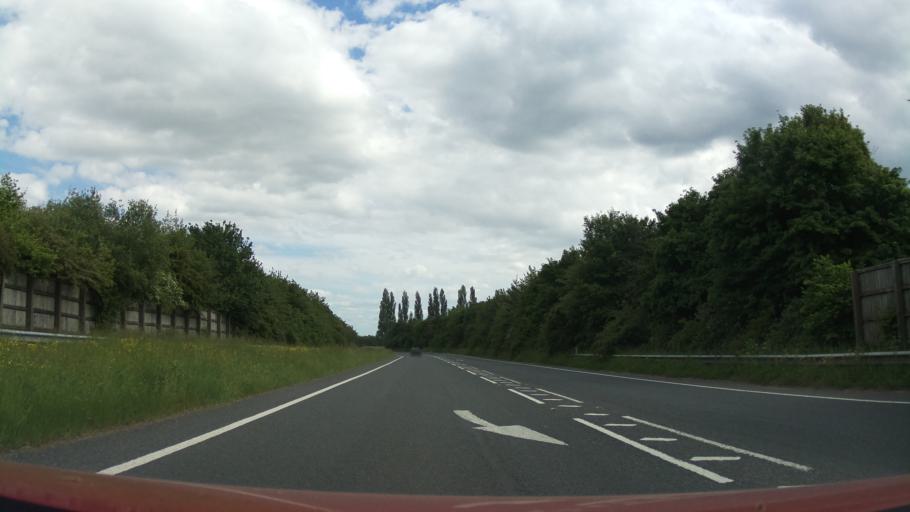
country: GB
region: England
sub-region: Worcestershire
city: Bransford
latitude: 52.1849
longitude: -2.2632
